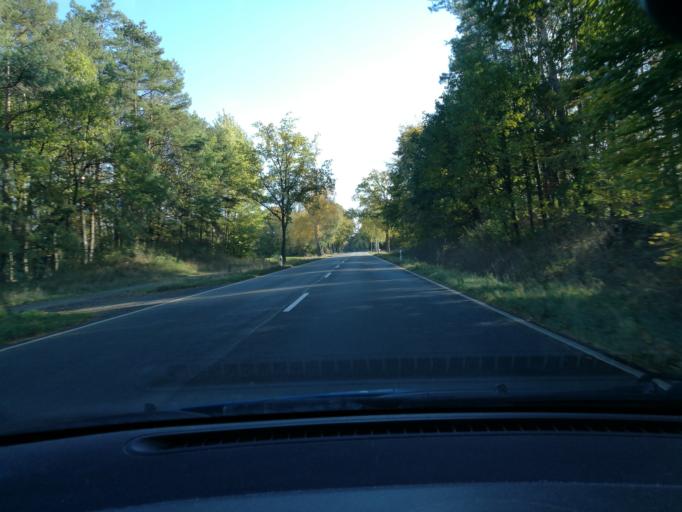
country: DE
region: Lower Saxony
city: Thomasburg
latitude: 53.1931
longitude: 10.6511
